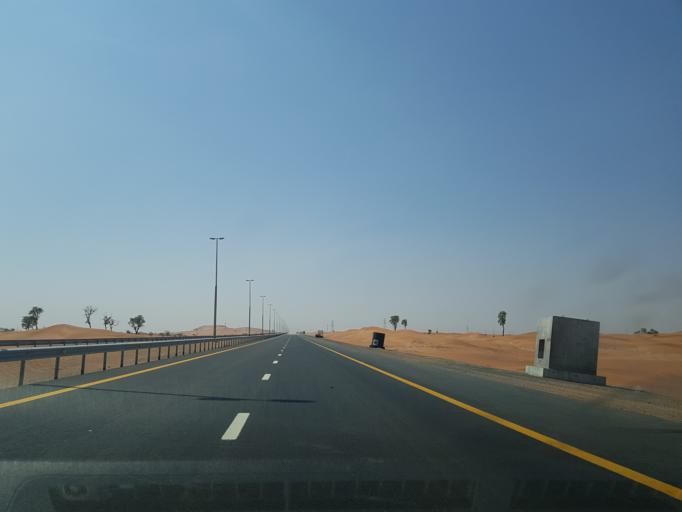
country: AE
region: Ash Shariqah
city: Adh Dhayd
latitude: 25.2429
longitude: 55.8684
